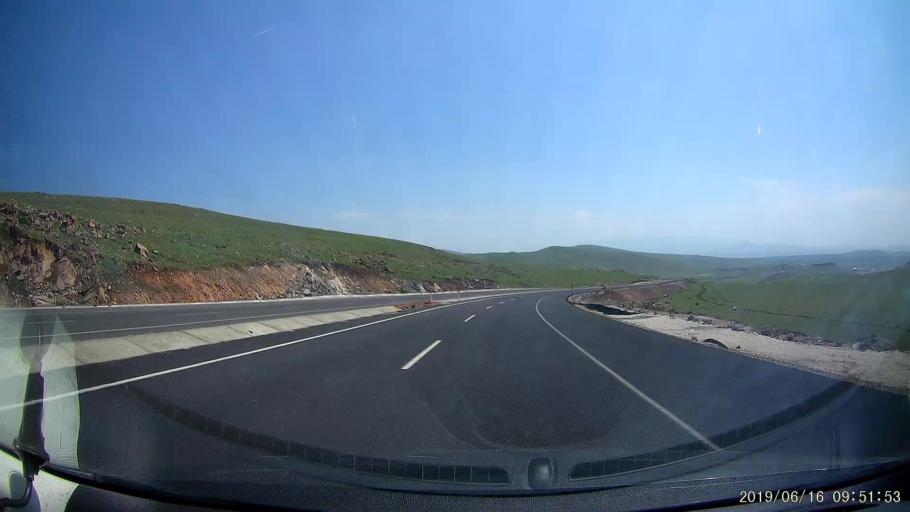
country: TR
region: Kars
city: Digor
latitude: 40.3919
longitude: 43.3744
